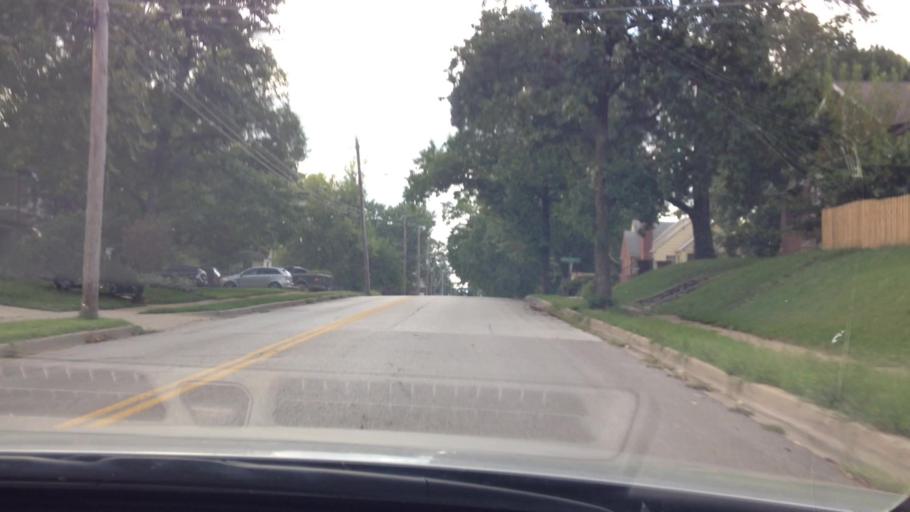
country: US
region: Kansas
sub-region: Johnson County
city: Mission Hills
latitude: 39.0197
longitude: -94.5653
